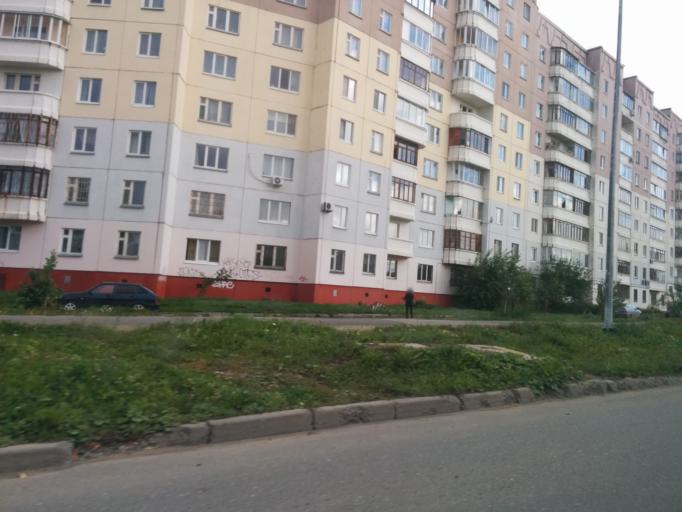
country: RU
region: Perm
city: Perm
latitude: 58.0042
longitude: 56.2973
